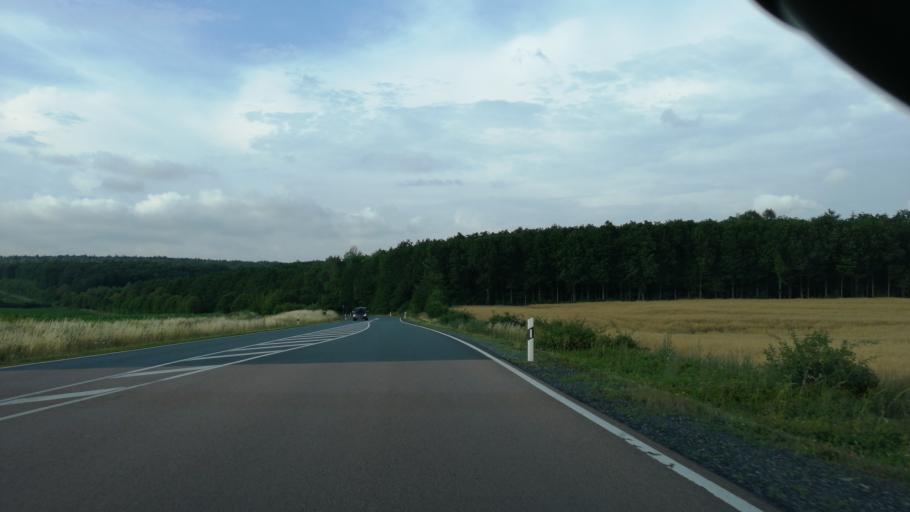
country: DE
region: Saxony-Anhalt
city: Riestedt
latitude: 51.5186
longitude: 11.3780
